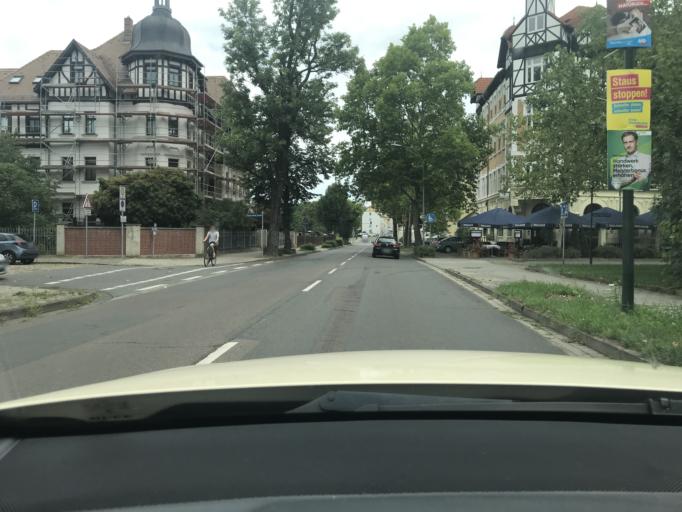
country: DE
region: Saxony
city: Markkleeberg
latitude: 51.2771
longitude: 12.3581
